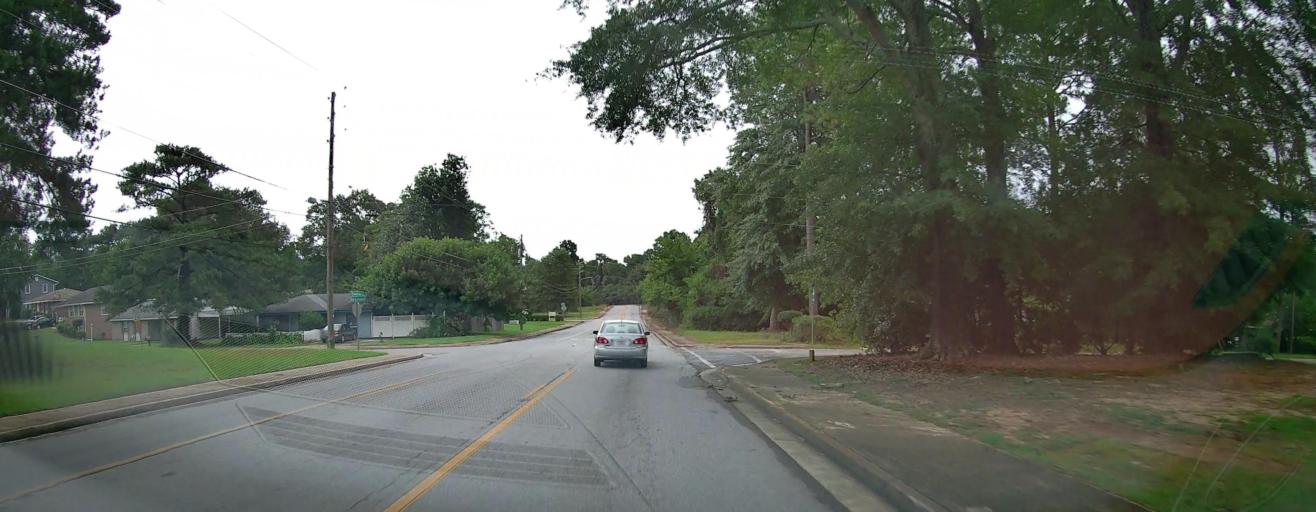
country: US
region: Georgia
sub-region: Bibb County
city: Macon
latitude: 32.7966
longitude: -83.6983
